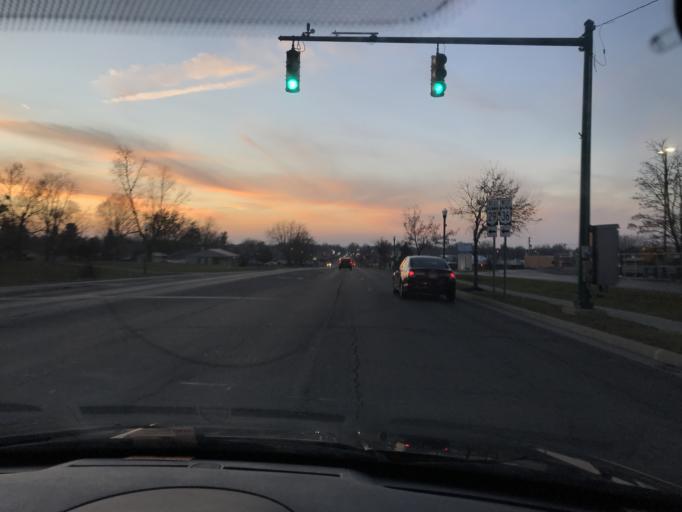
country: US
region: Ohio
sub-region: Champaign County
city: Urbana
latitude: 40.1067
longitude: -83.7293
